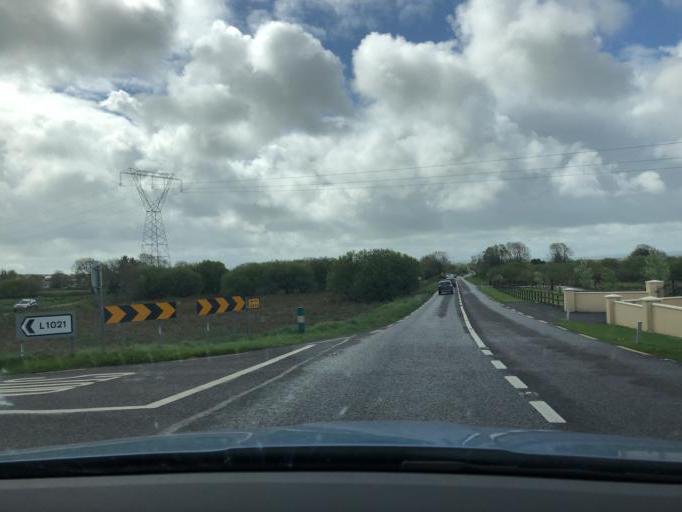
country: IE
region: Munster
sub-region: An Clar
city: Kilrush
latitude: 52.5430
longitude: -9.3825
